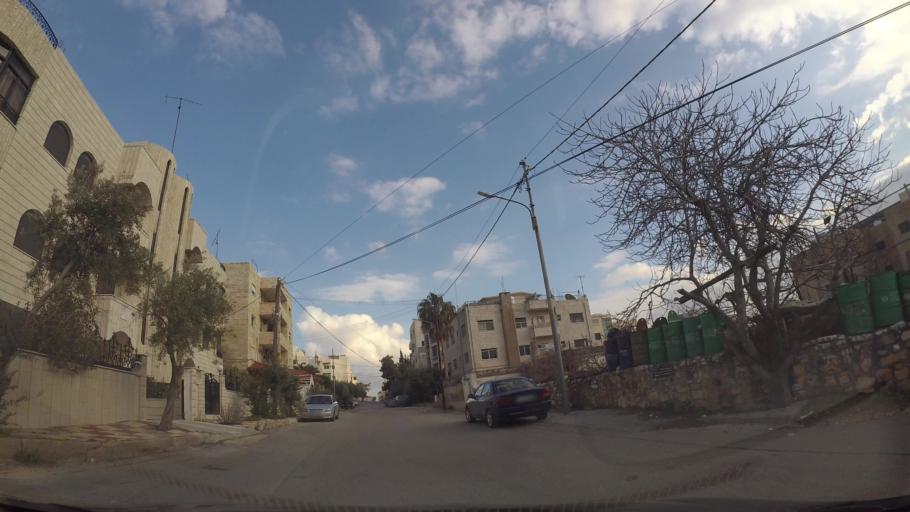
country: JO
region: Amman
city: Al Bunayyat ash Shamaliyah
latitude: 31.9113
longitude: 35.8823
